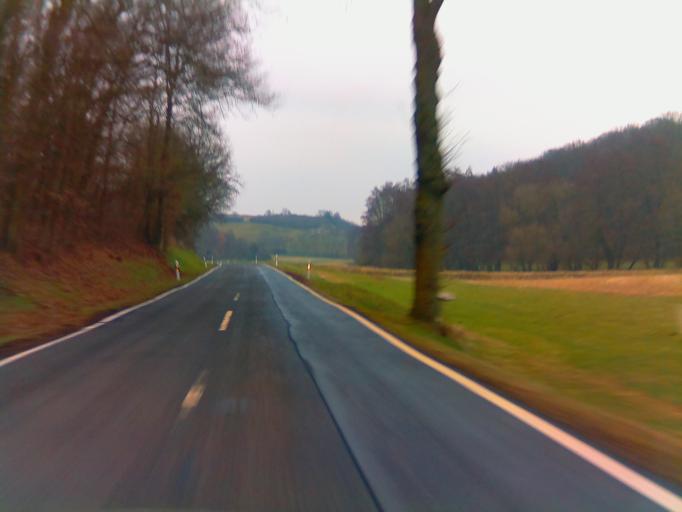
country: DE
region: Rheinland-Pfalz
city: Stein-Bockenheim
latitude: 49.7559
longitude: 7.9605
